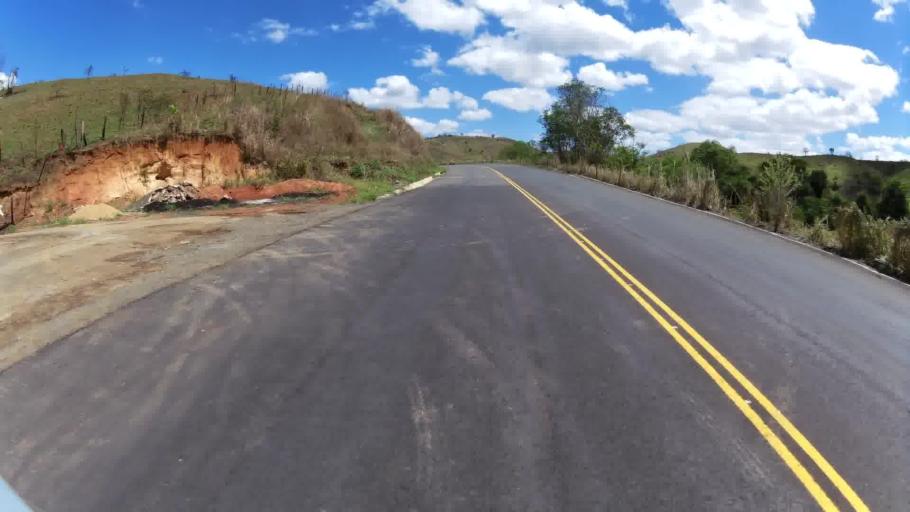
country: BR
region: Rio de Janeiro
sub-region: Itaperuna
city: Itaperuna
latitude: -21.3296
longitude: -41.8812
